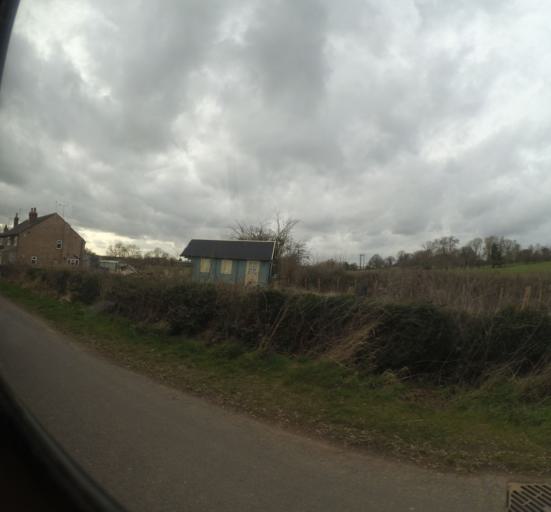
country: GB
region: England
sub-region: Warwickshire
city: Brandon
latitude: 52.4102
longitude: -1.3552
